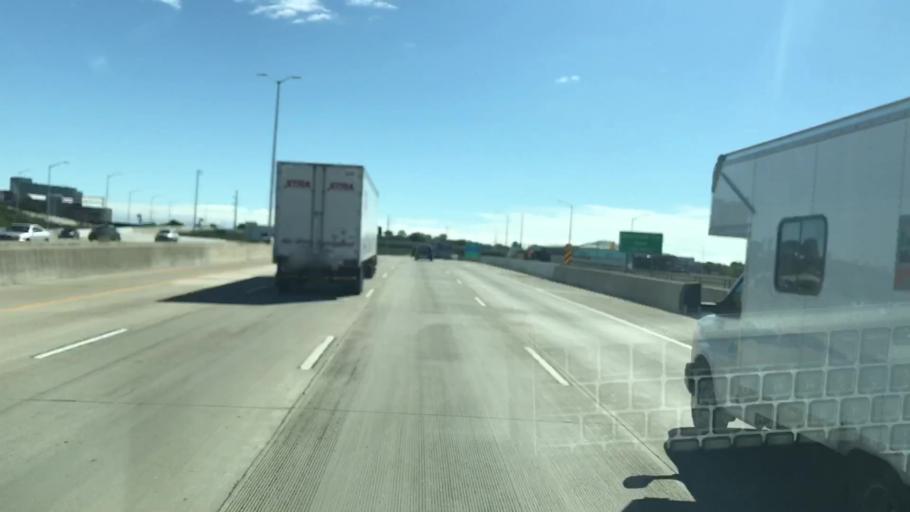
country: US
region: Wisconsin
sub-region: Milwaukee County
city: Wauwatosa
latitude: 43.0462
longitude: -88.0371
